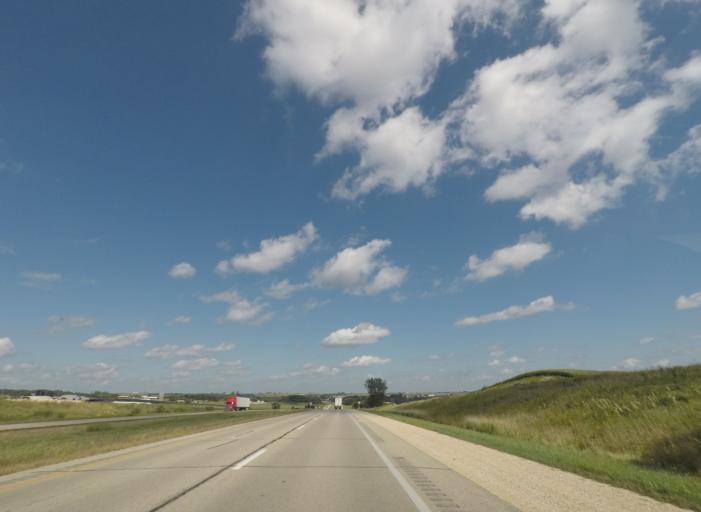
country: US
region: Iowa
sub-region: Dubuque County
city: Cascade
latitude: 42.3160
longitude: -90.9431
